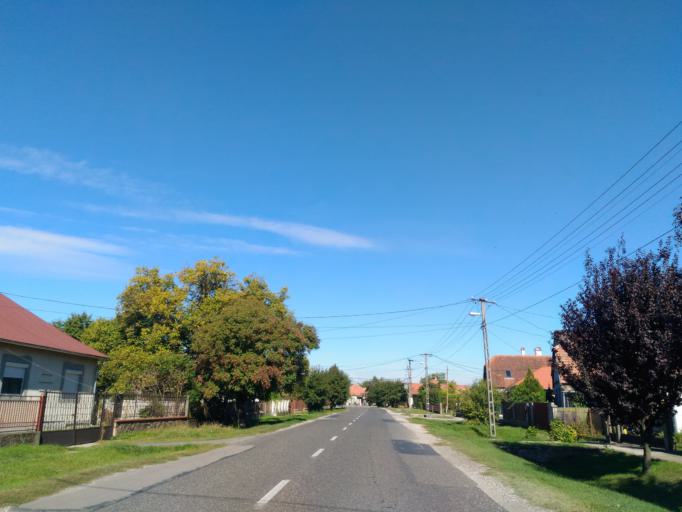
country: HU
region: Fejer
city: Ivancsa
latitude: 47.1603
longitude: 18.8272
